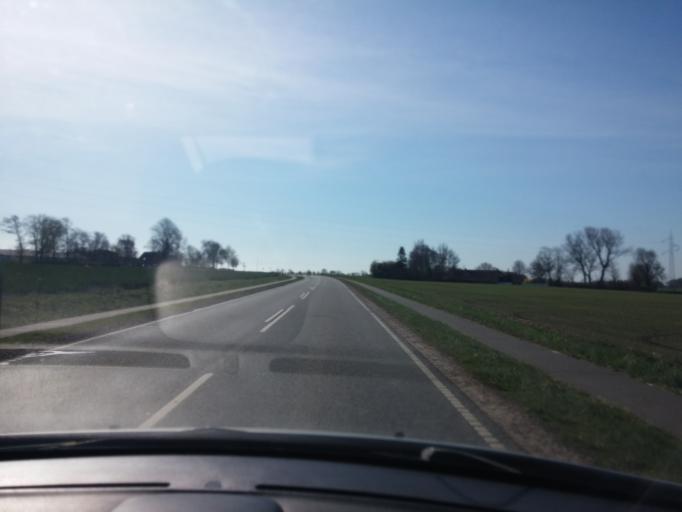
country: DK
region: Central Jutland
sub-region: Odder Kommune
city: Odder
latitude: 55.9433
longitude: 10.2089
